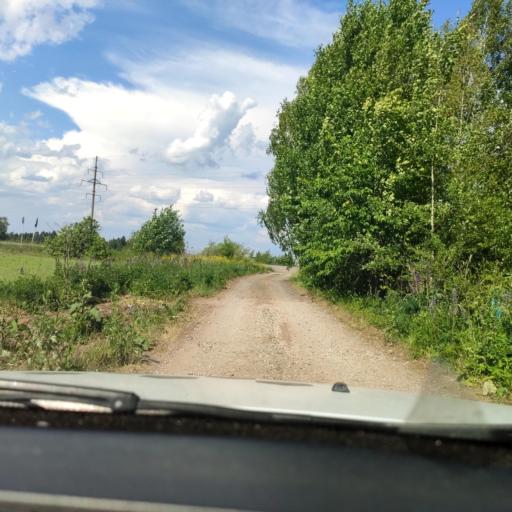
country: RU
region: Perm
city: Novyye Lyady
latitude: 58.1321
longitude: 56.4812
